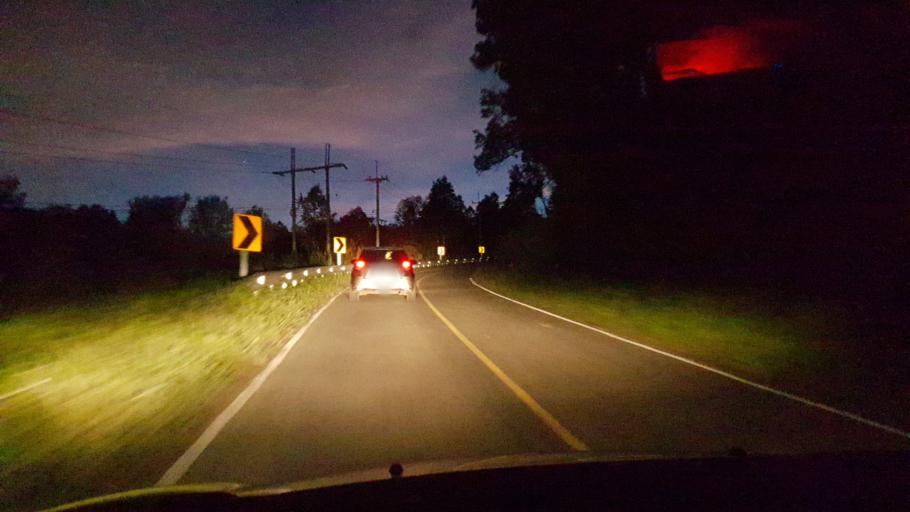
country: TH
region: Mae Hong Son
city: Khun Yuam
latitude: 18.7713
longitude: 98.1621
